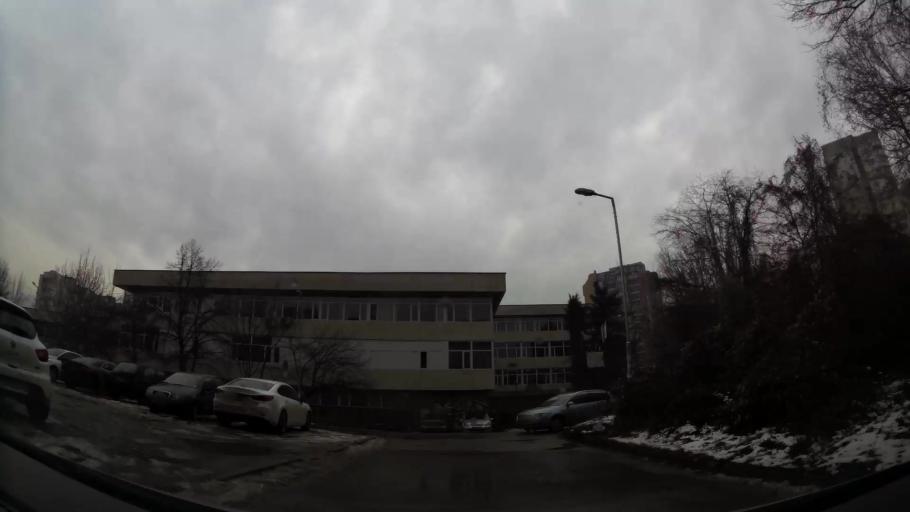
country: BG
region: Sofia-Capital
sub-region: Stolichna Obshtina
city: Sofia
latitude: 42.6732
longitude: 23.2840
